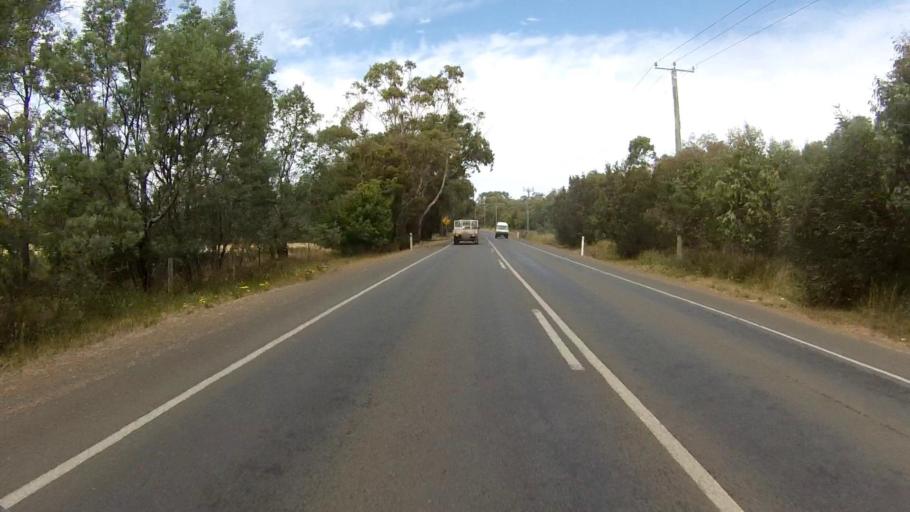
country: AU
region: Tasmania
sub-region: Clarence
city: Sandford
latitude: -42.9416
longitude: 147.4976
